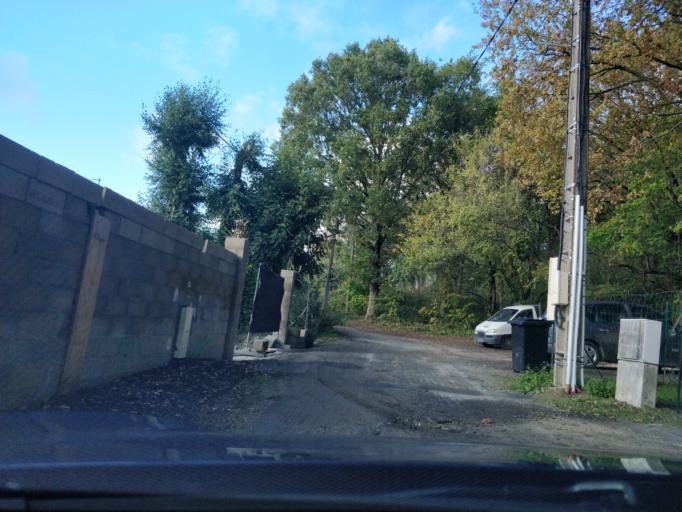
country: FR
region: Ile-de-France
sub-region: Departement de l'Essonne
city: Briis-sous-Forges
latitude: 48.6256
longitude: 2.1348
